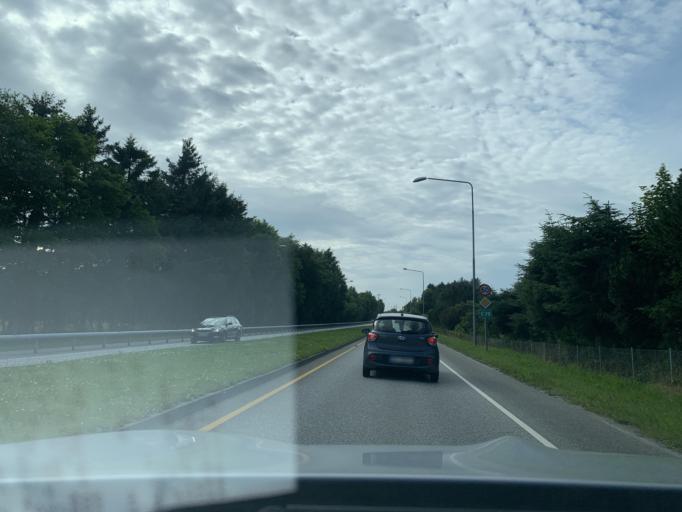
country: NO
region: Rogaland
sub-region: Stavanger
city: Stavanger
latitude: 58.9173
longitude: 5.7177
